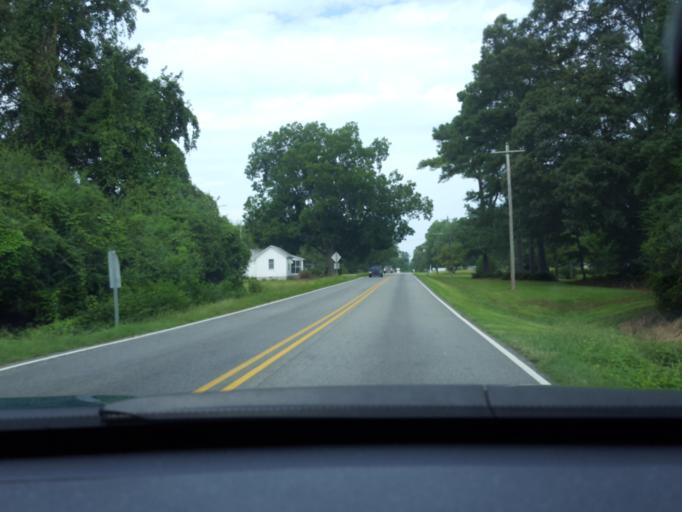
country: US
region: North Carolina
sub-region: Chowan County
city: Edenton
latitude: 36.1002
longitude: -76.6296
